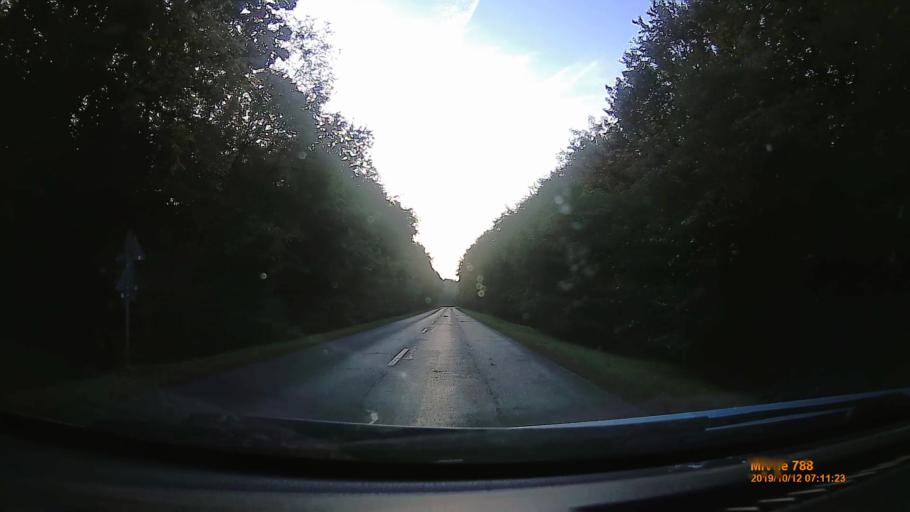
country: HU
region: Hajdu-Bihar
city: Mikepercs
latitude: 47.4609
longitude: 21.6772
